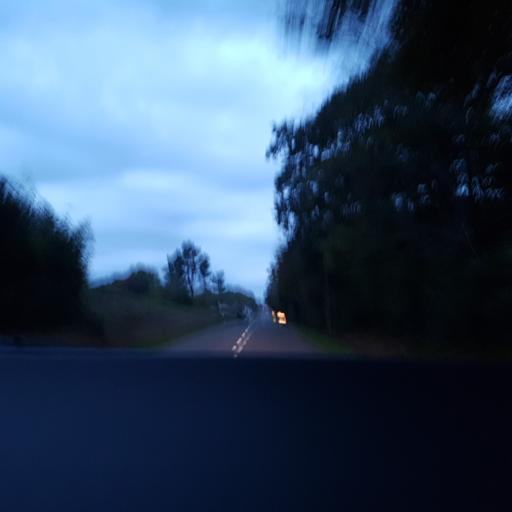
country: FR
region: Aquitaine
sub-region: Departement des Landes
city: Gabarret
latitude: 43.9474
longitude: 0.0220
